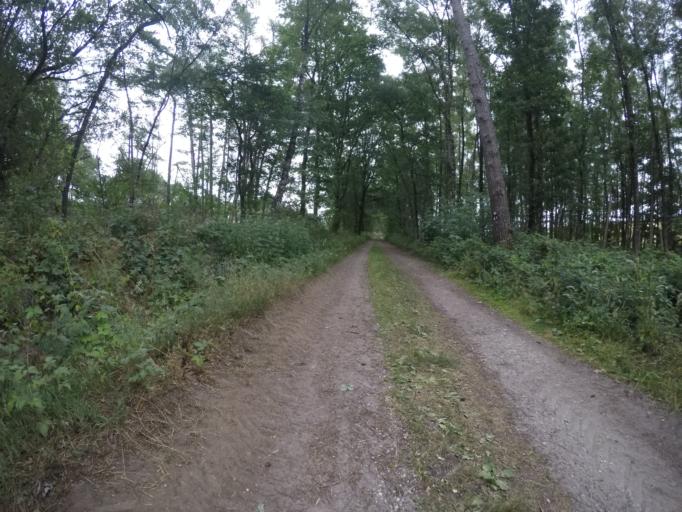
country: DE
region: North Rhine-Westphalia
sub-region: Regierungsbezirk Dusseldorf
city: Bocholt
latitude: 51.8056
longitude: 6.6194
